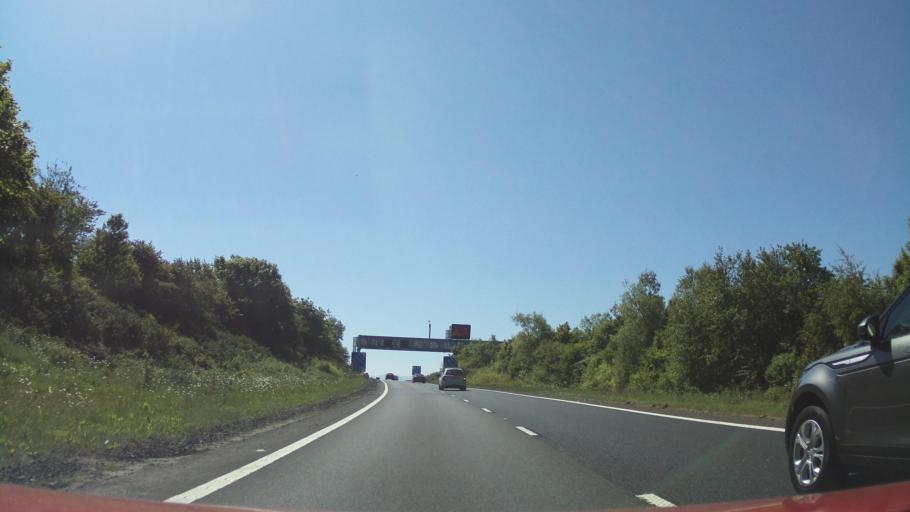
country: GB
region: Scotland
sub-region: Fife
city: Crossgates
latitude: 56.0772
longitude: -3.3912
